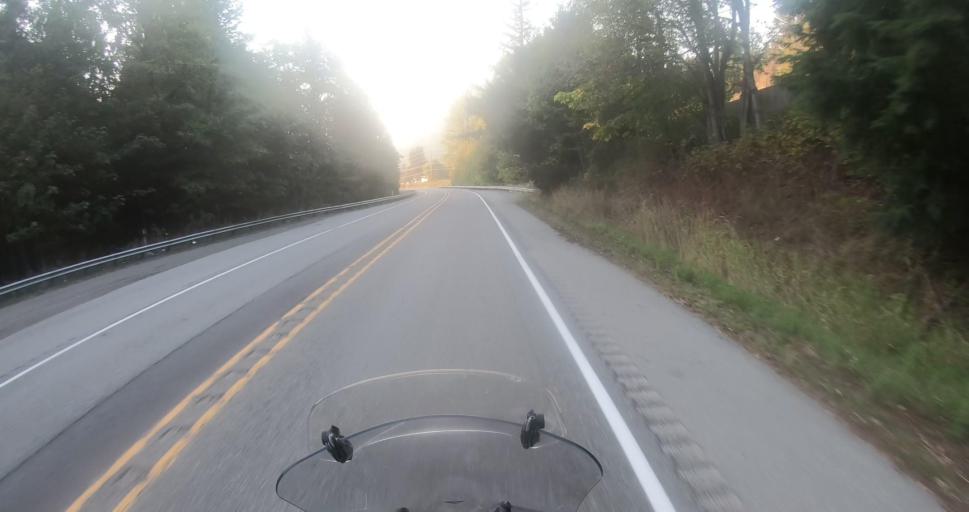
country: US
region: Washington
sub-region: Lewis County
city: Morton
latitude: 46.5382
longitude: -121.9824
